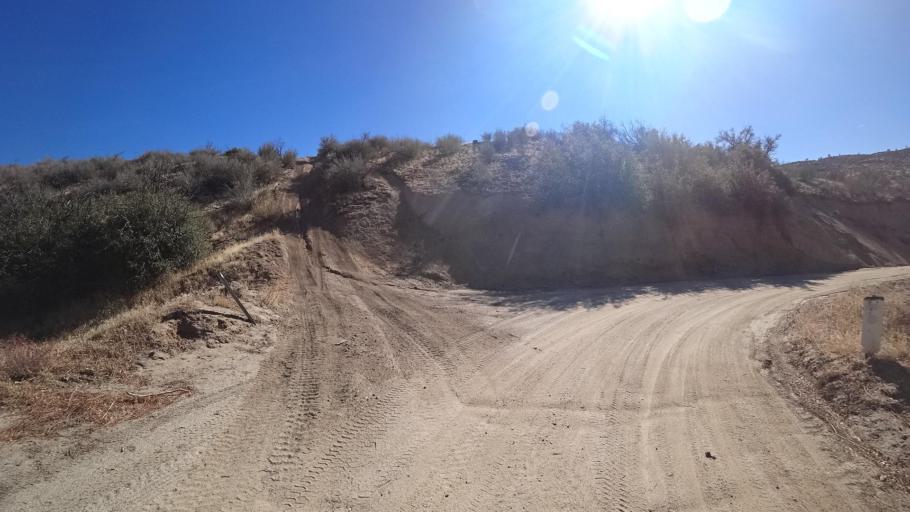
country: US
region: California
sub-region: Kern County
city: Wofford Heights
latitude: 35.7039
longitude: -118.4932
